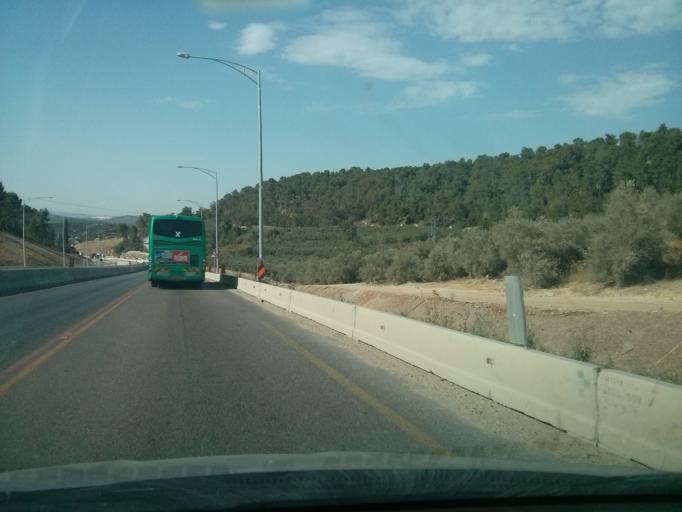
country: IL
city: Mevo horon
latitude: 31.7922
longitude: 35.0143
